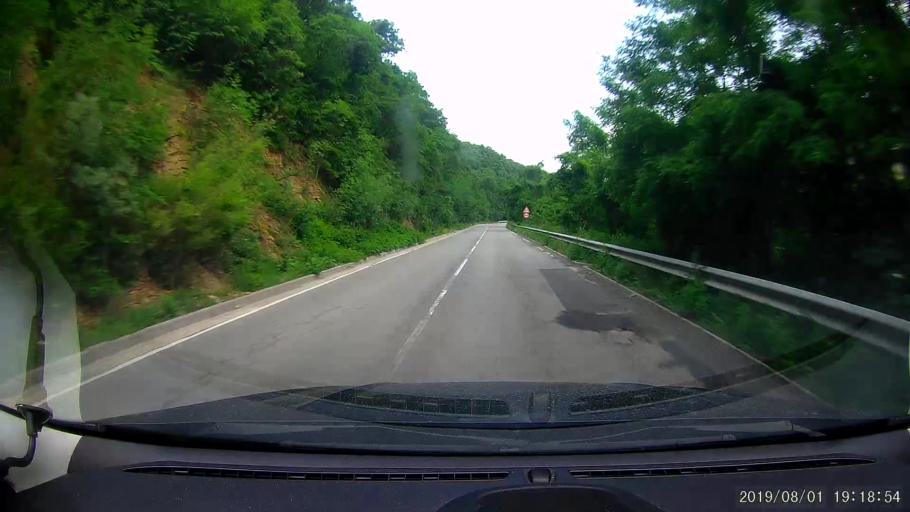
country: BG
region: Shumen
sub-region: Obshtina Smyadovo
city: Smyadovo
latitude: 42.9063
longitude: 26.9406
